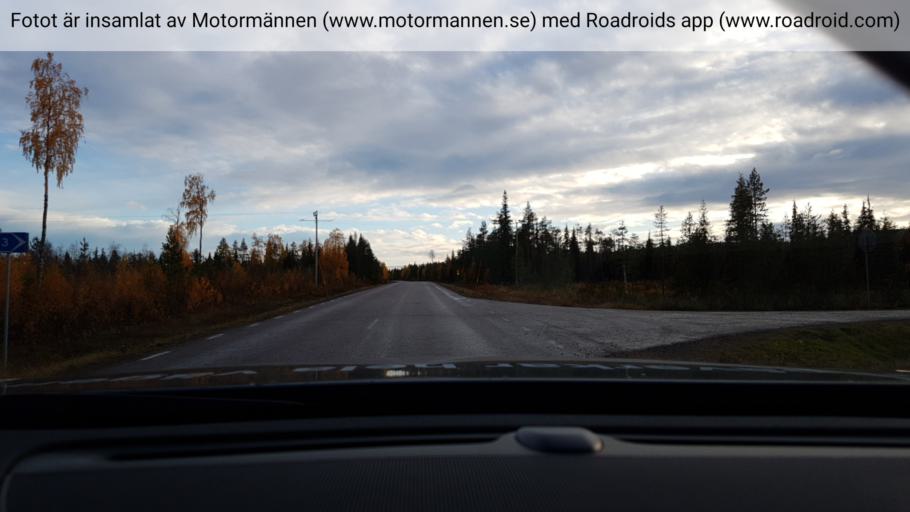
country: SE
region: Norrbotten
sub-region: Overkalix Kommun
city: OEverkalix
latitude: 66.8687
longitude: 22.7571
